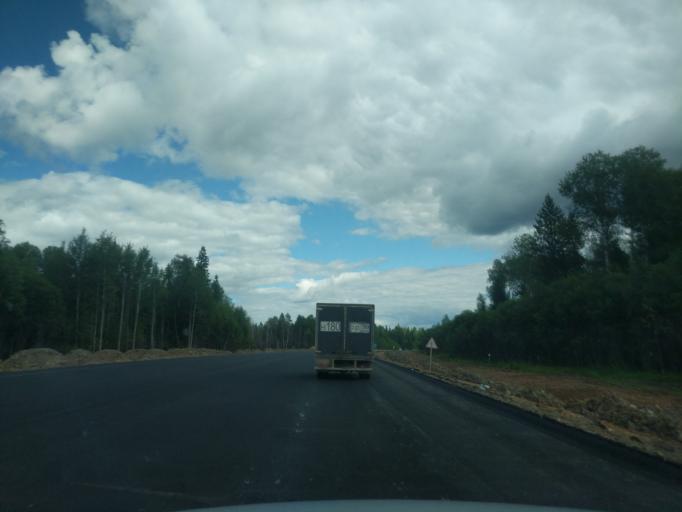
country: RU
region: Kostroma
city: Sudislavl'
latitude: 57.8258
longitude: 41.5018
